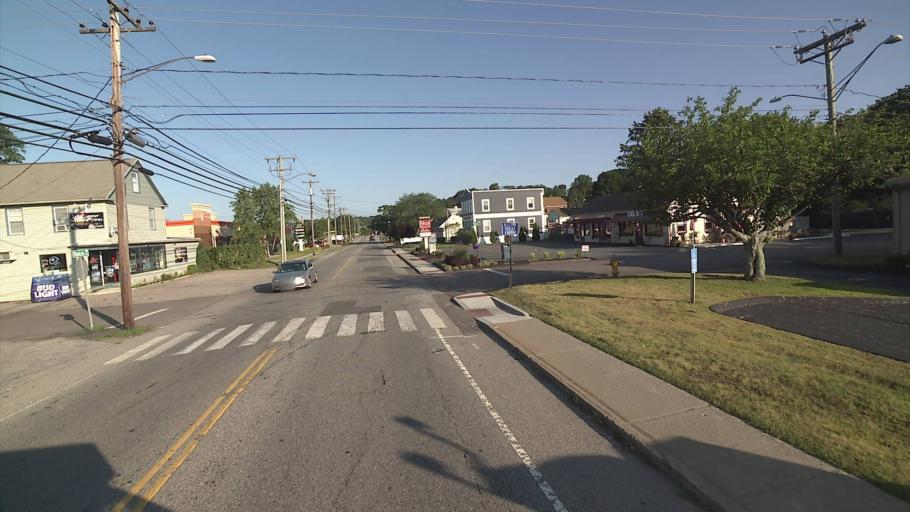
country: US
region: Connecticut
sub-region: New London County
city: Mystic
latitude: 41.3488
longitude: -71.9571
